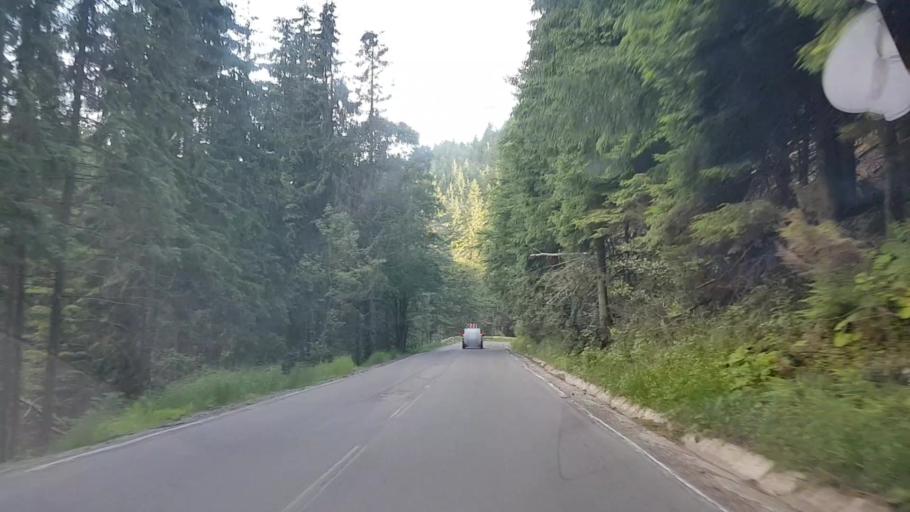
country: RO
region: Harghita
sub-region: Comuna Varsag
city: Varsag
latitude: 46.6360
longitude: 25.2656
